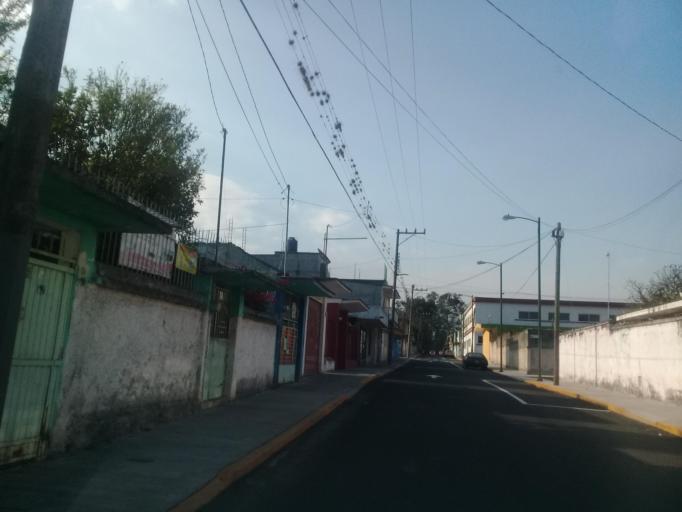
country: MX
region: Veracruz
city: Orizaba
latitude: 18.8521
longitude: -97.1124
